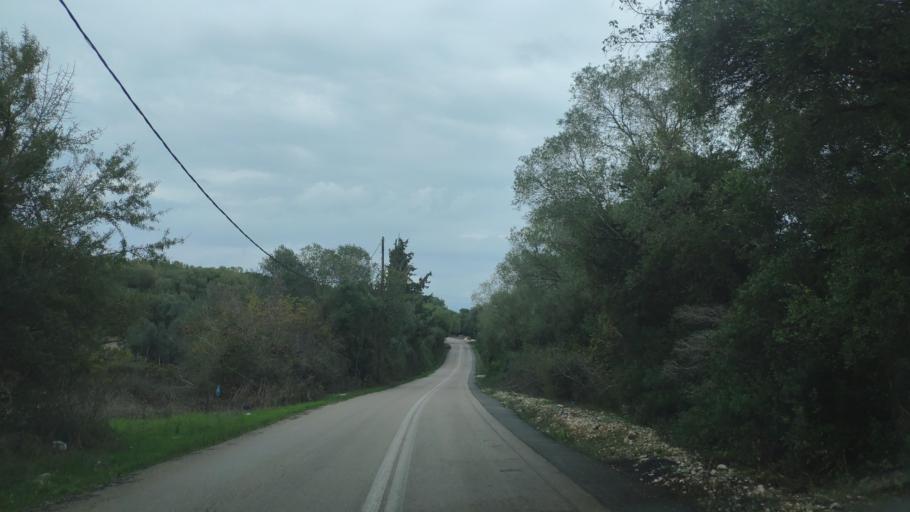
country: GR
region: West Greece
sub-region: Nomos Aitolias kai Akarnanias
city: Vonitsa
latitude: 38.9235
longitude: 20.8592
